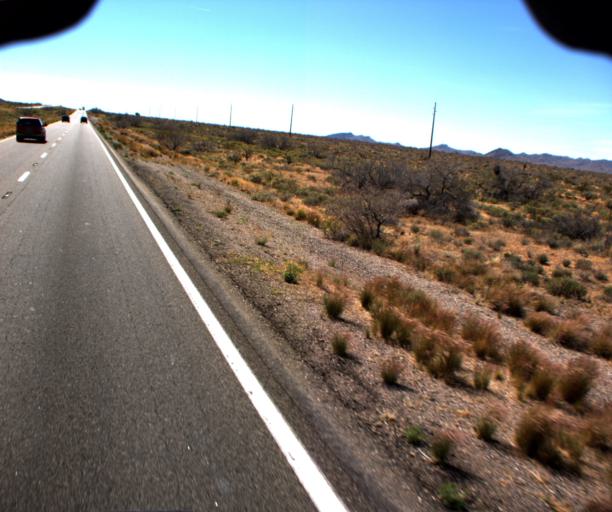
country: US
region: Arizona
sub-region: Mohave County
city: Dolan Springs
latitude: 35.4528
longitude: -114.2995
